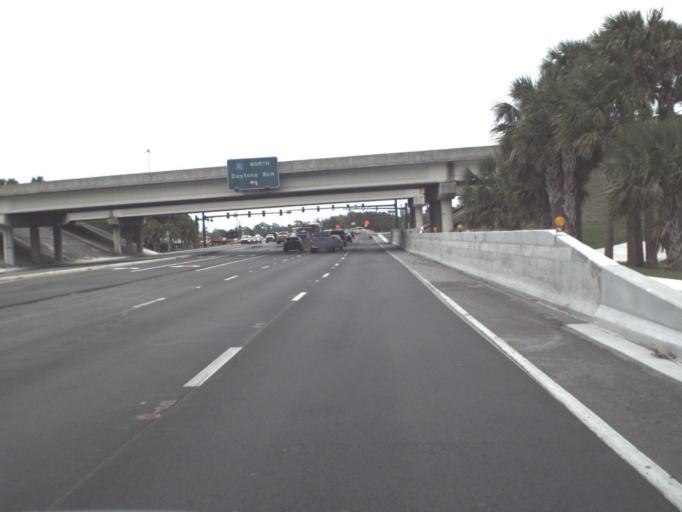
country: US
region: Florida
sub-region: Martin County
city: Palm City
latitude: 27.1080
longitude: -80.2613
